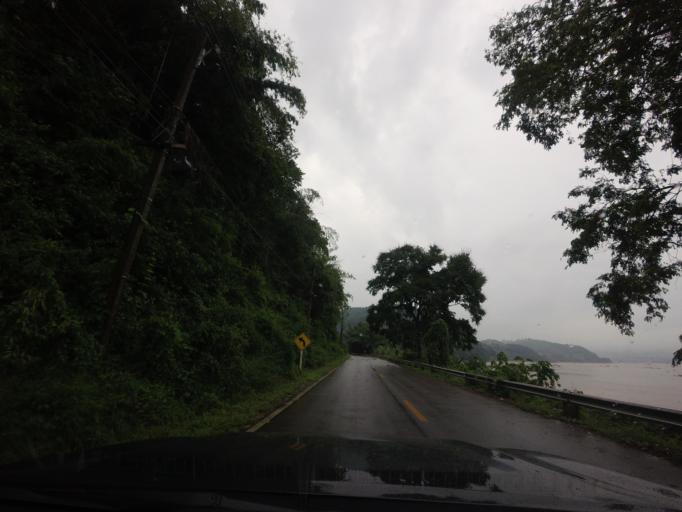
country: TH
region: Nong Khai
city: Sangkhom
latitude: 18.2066
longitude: 102.1228
